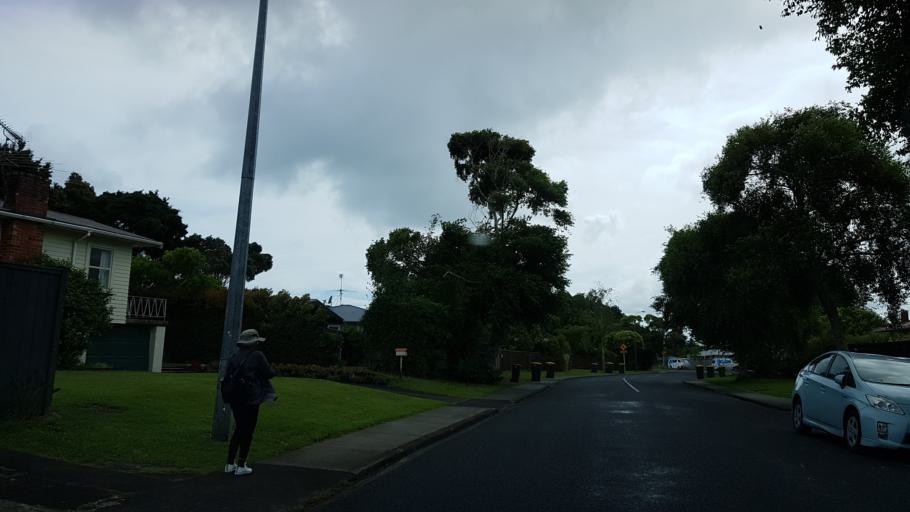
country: NZ
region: Auckland
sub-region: Auckland
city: North Shore
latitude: -36.7939
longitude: 174.7397
